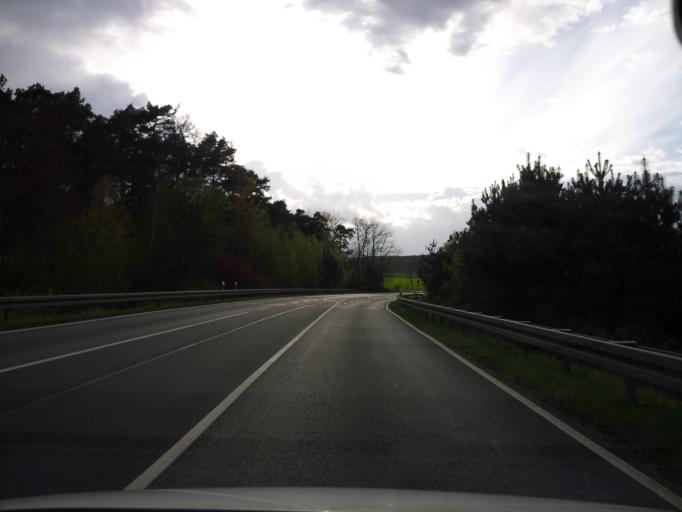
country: DE
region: Brandenburg
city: Guben
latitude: 51.9029
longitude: 14.6901
